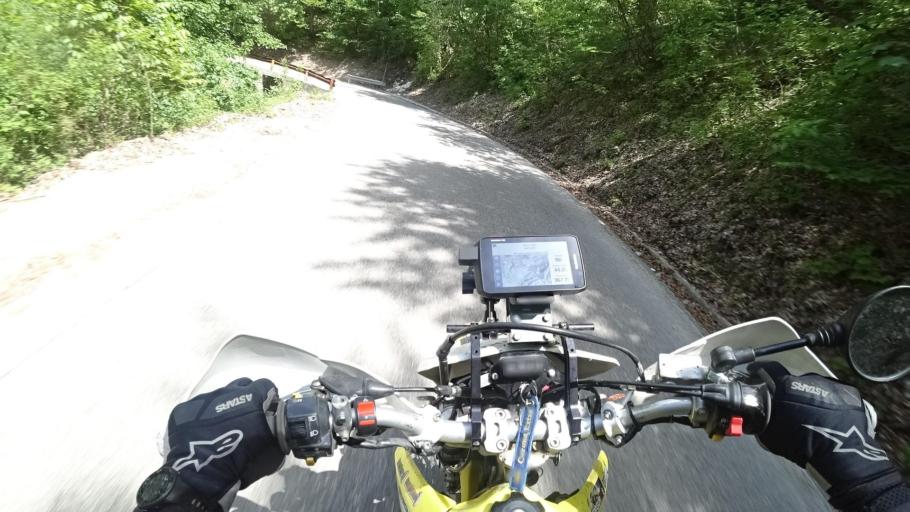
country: BA
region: Federation of Bosnia and Herzegovina
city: Polje-Bijela
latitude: 43.6131
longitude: 17.9812
